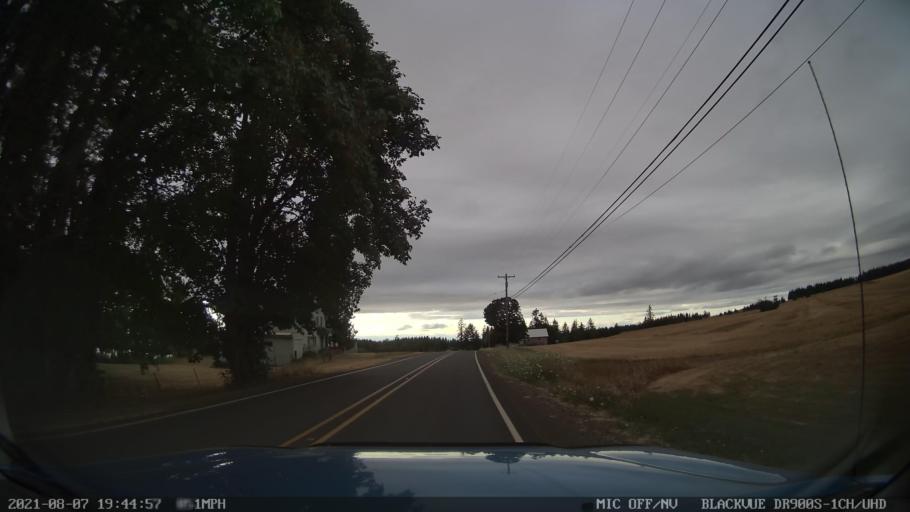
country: US
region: Oregon
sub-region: Marion County
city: Silverton
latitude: 44.9438
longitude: -122.6901
